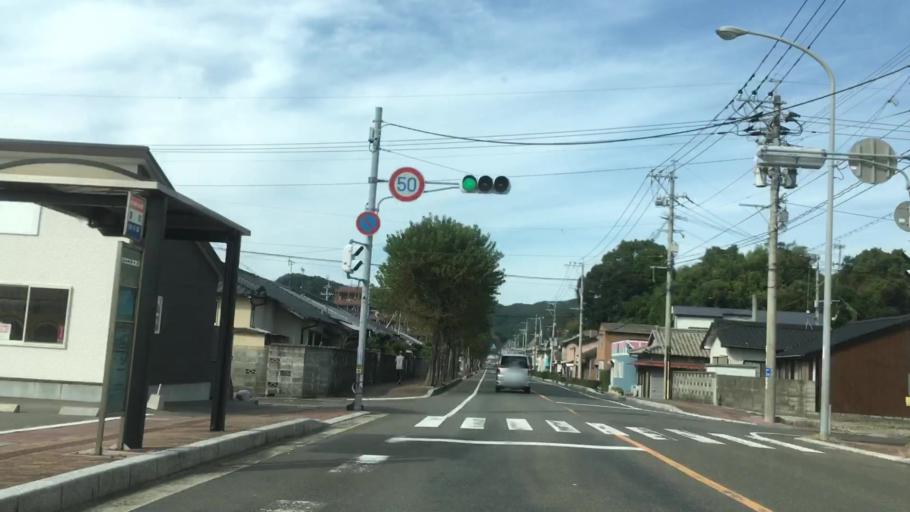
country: JP
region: Nagasaki
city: Sasebo
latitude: 33.0356
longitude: 129.6223
